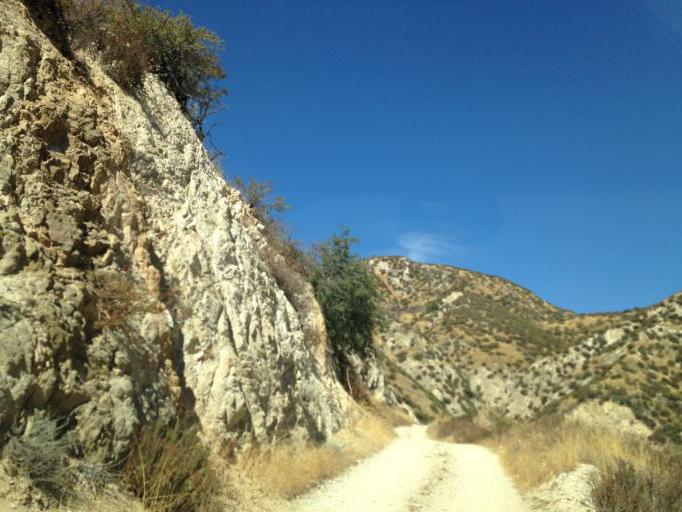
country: US
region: California
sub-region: San Bernardino County
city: Running Springs
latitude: 34.1359
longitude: -117.1016
